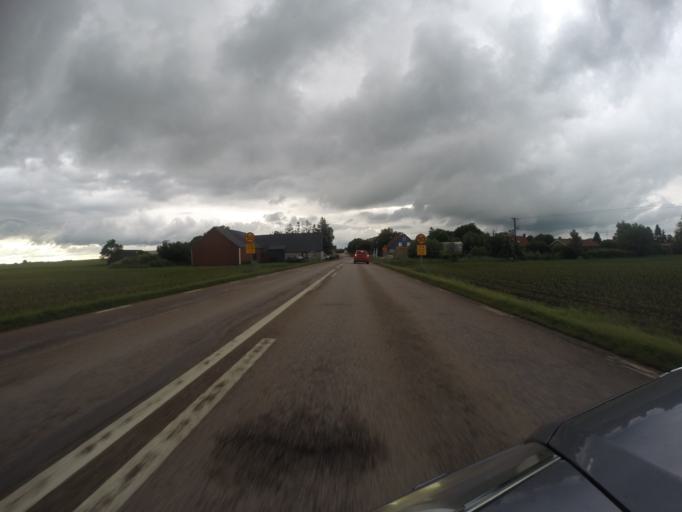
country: SE
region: Skane
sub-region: Landskrona
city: Asmundtorp
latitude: 55.9537
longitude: 12.9464
